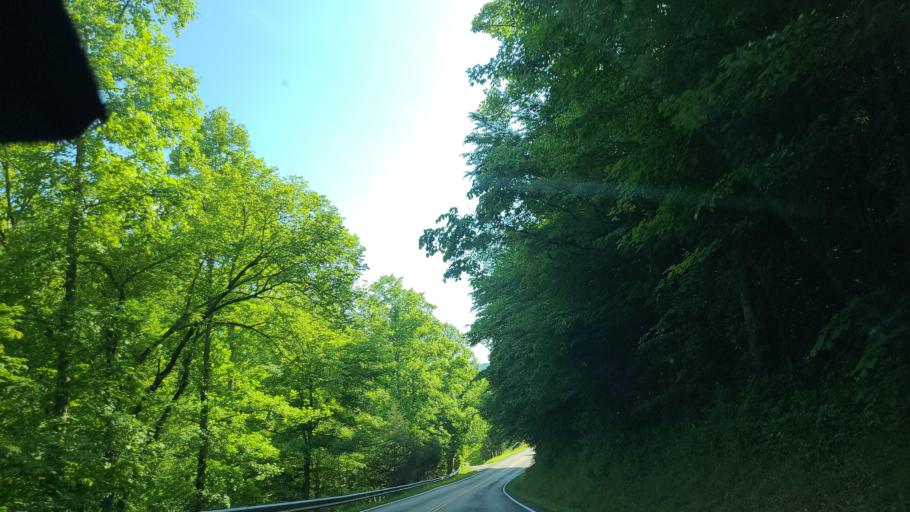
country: US
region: Kentucky
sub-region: Bell County
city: Pineville
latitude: 36.7437
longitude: -83.7958
